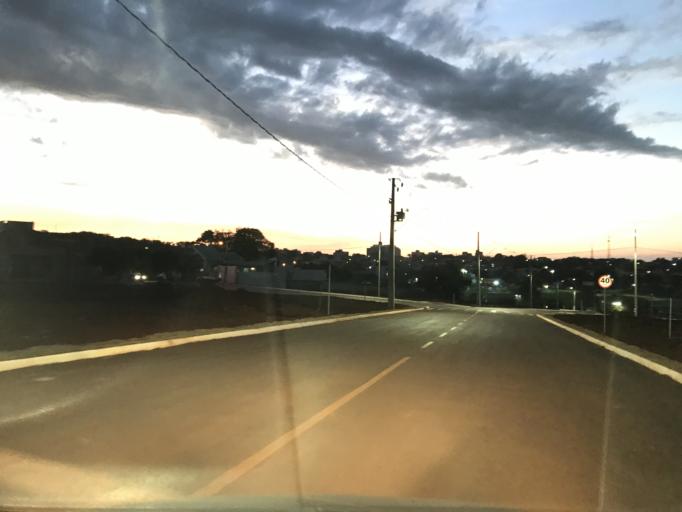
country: BR
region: Parana
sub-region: Palotina
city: Palotina
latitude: -24.2910
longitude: -53.8296
